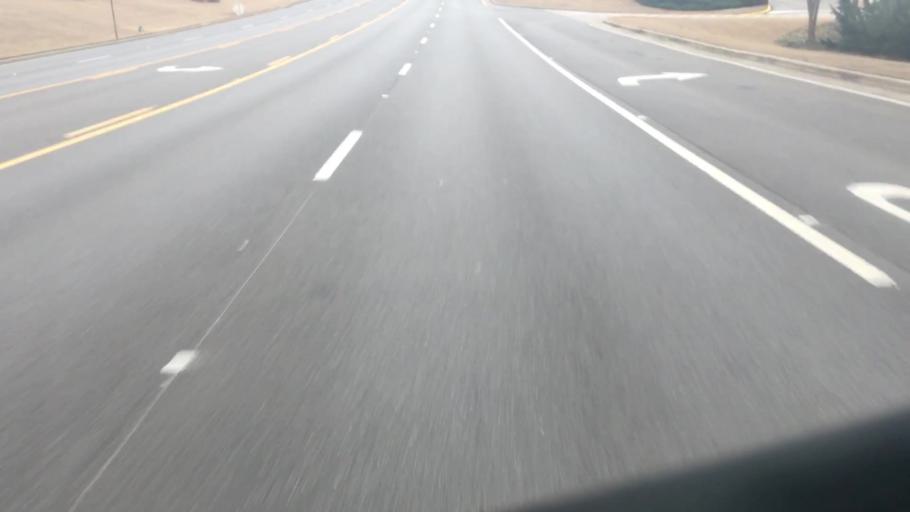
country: US
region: Alabama
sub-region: Jefferson County
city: Hoover
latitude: 33.3549
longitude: -86.8410
